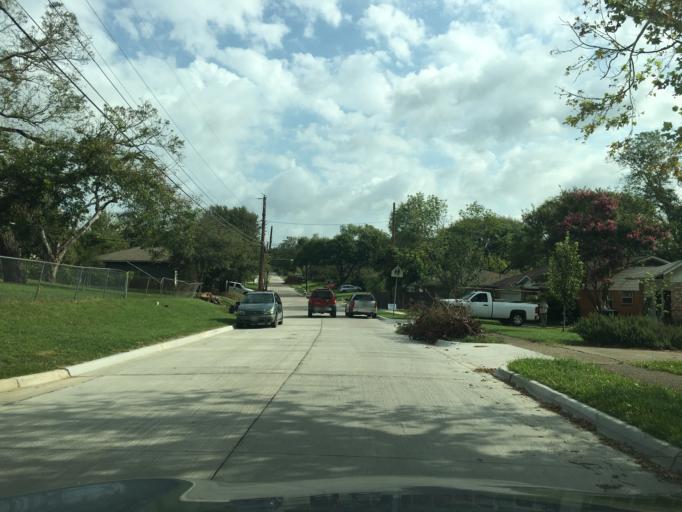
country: US
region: Texas
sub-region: Dallas County
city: Richardson
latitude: 32.9012
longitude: -96.7513
